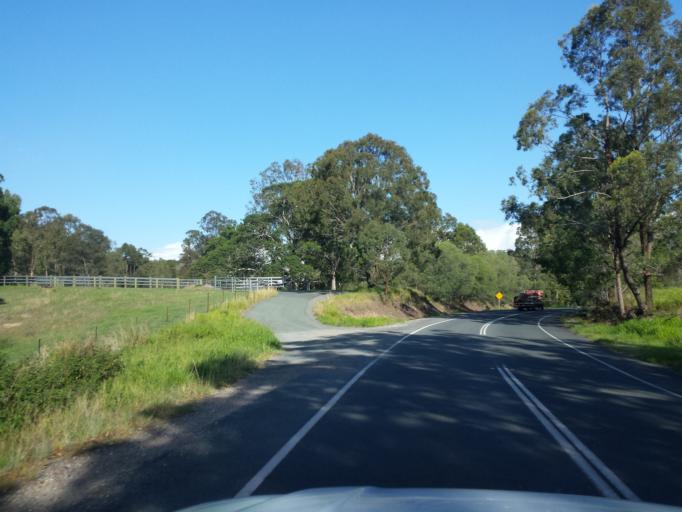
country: AU
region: Queensland
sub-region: Logan
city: Windaroo
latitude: -27.7641
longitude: 153.1870
